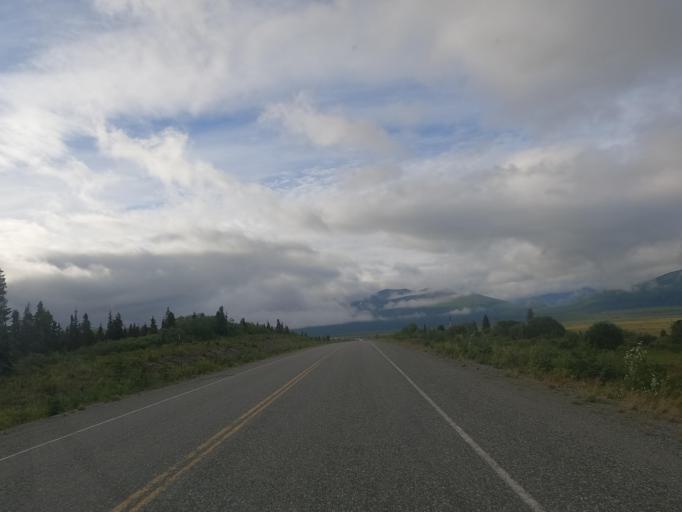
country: CA
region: Yukon
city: Haines Junction
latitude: 59.9400
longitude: -136.7998
